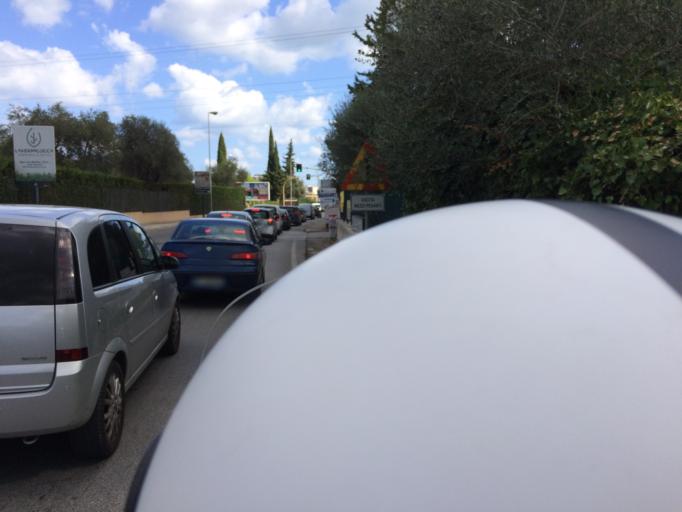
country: IT
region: Apulia
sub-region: Provincia di Bari
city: Bari
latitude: 41.0994
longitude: 16.8453
